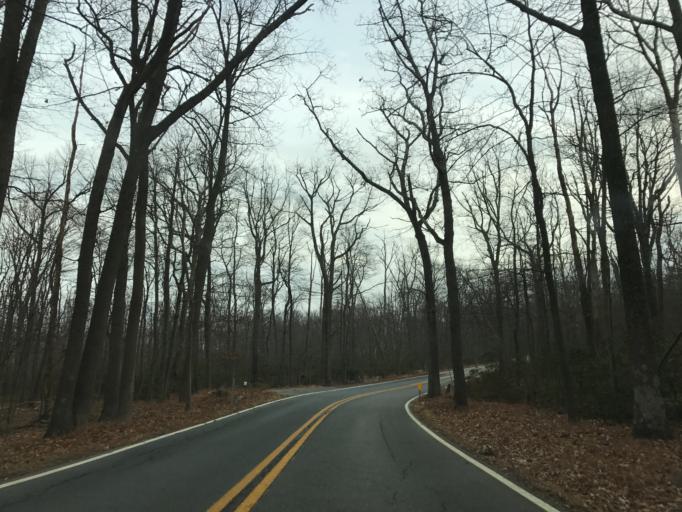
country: US
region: Maryland
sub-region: Frederick County
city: Braddock Heights
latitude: 39.4787
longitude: -77.4928
